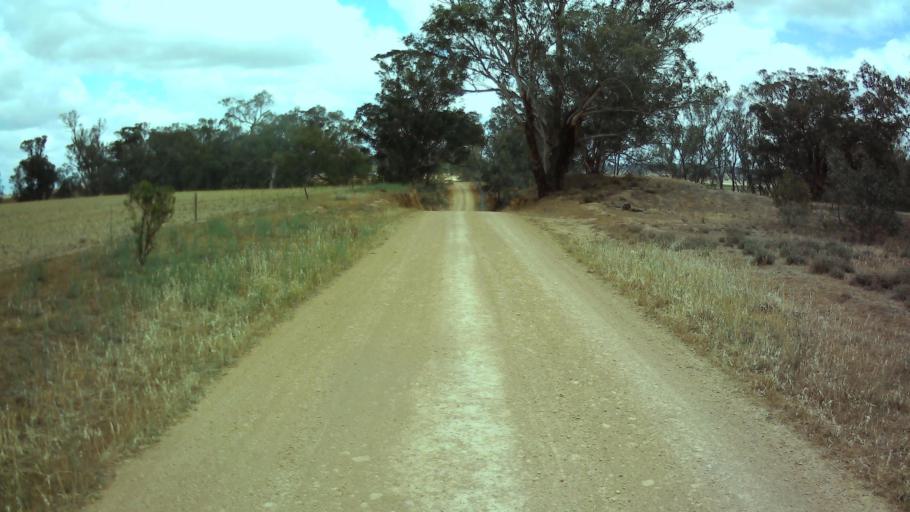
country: AU
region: New South Wales
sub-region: Weddin
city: Grenfell
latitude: -33.9794
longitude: 148.2676
